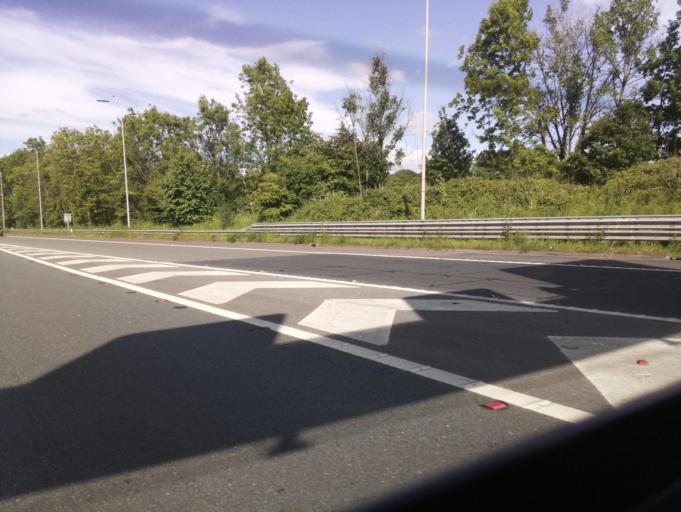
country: GB
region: England
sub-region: City and Borough of Salford
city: Walkden
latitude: 53.5049
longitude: -2.3789
